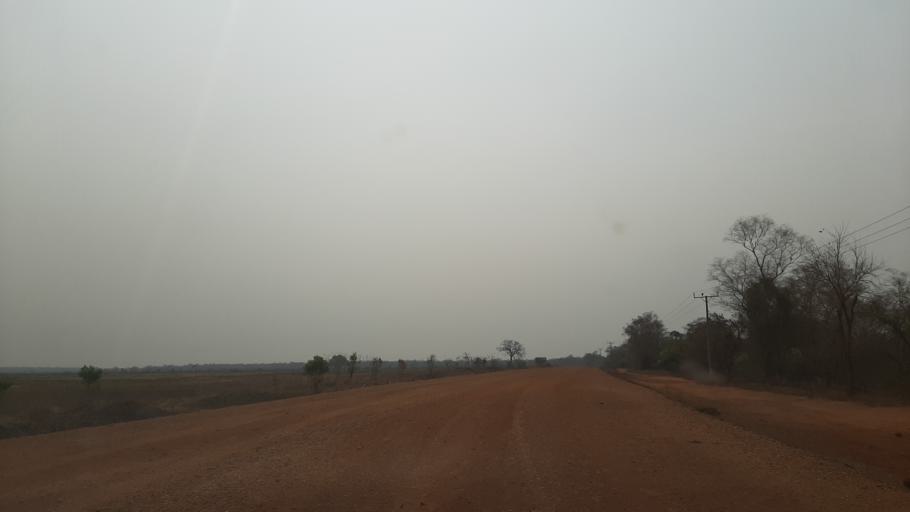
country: ET
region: Gambela
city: Gambela
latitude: 8.1630
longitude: 34.3203
